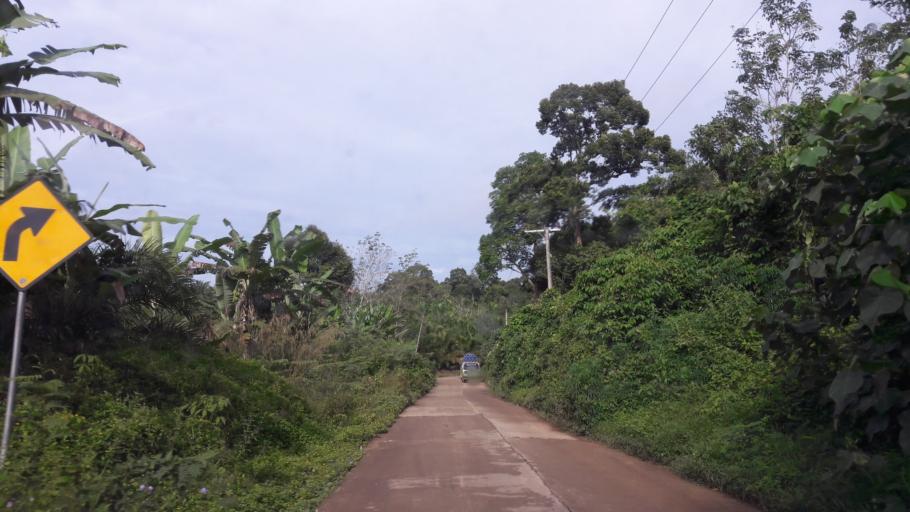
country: ID
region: South Sumatra
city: Gunungmegang Dalam
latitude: -3.2812
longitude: 103.7583
